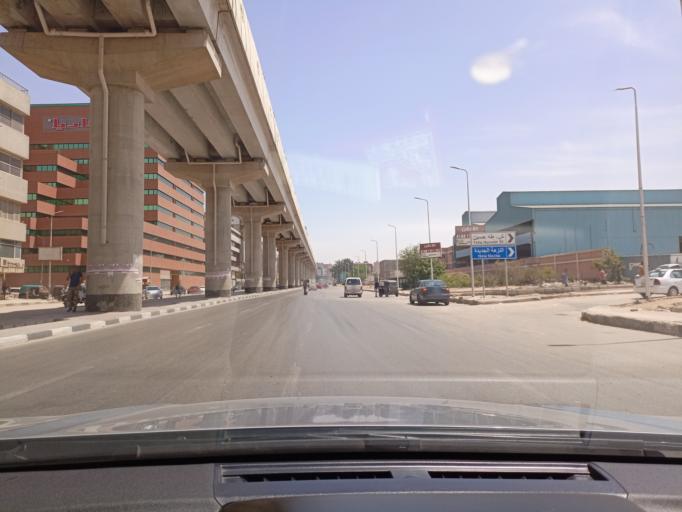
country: EG
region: Muhafazat al Qalyubiyah
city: Al Khankah
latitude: 30.1320
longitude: 31.3765
